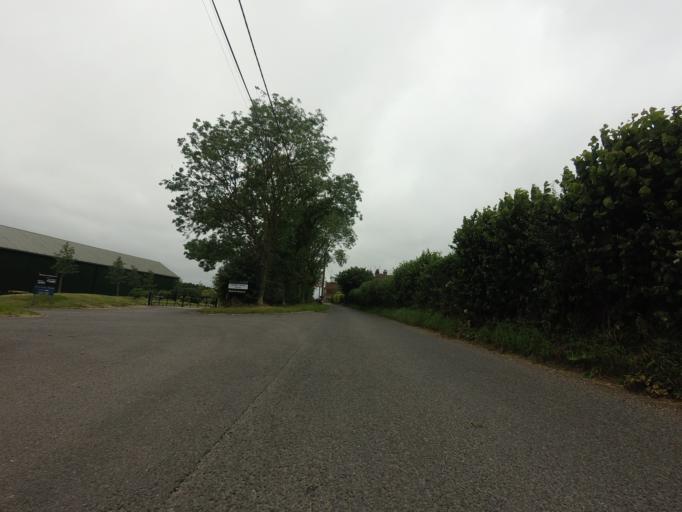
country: GB
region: England
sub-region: Kent
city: Borough Green
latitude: 51.3069
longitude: 0.2702
